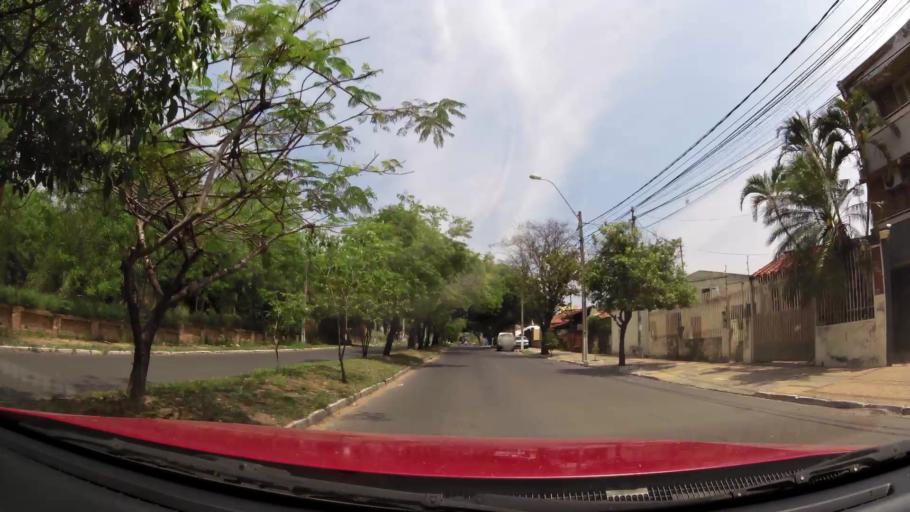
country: PY
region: Asuncion
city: Asuncion
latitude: -25.2681
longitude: -57.5974
